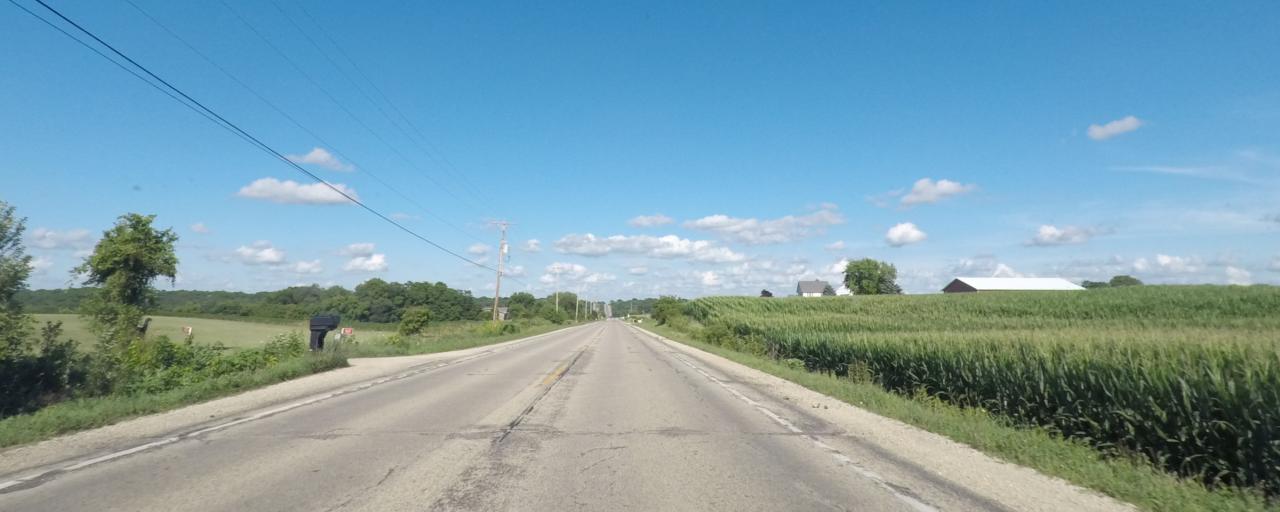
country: US
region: Wisconsin
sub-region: Rock County
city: Janesville
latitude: 42.7303
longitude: -89.0756
